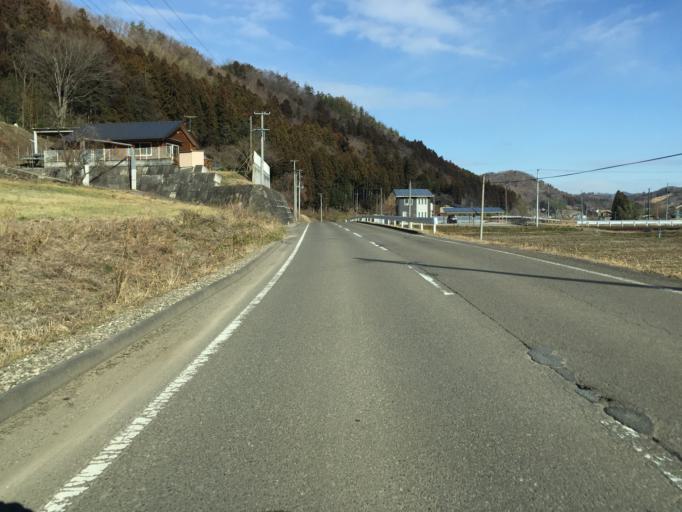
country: JP
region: Fukushima
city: Hobaramachi
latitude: 37.7569
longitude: 140.5694
